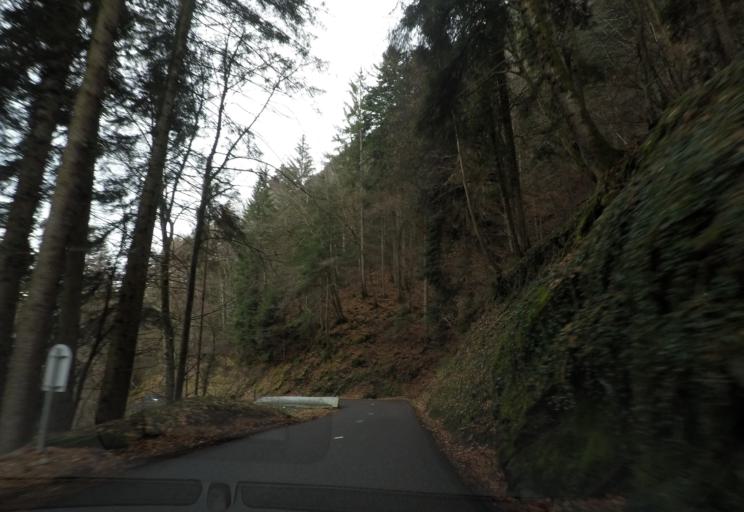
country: FR
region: Rhone-Alpes
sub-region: Departement de la Haute-Savoie
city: Ayse
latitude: 46.0563
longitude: 6.4376
